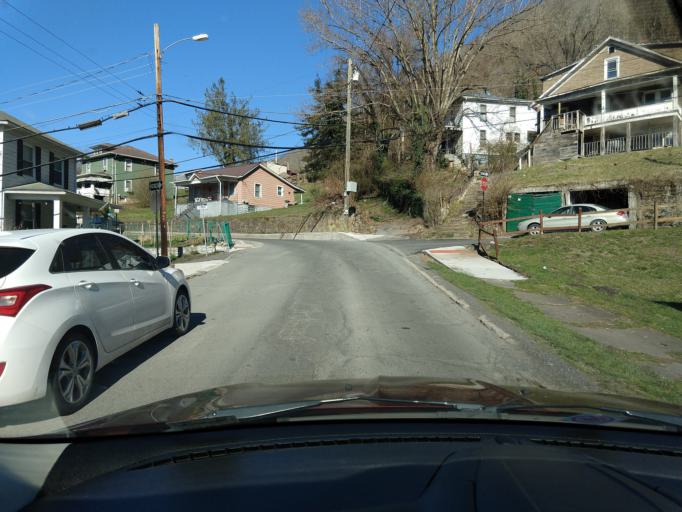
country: US
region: West Virginia
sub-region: Summers County
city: Hinton
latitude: 37.6797
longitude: -80.8781
